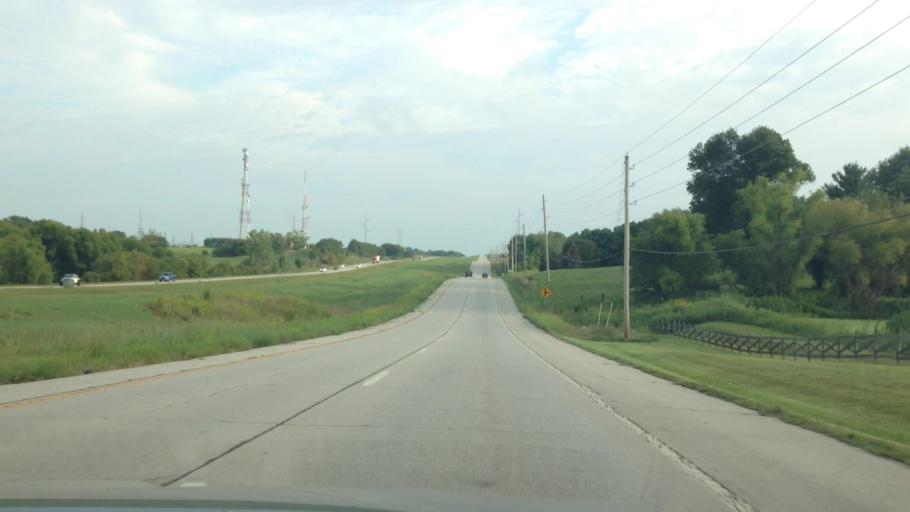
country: US
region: Missouri
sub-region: Clay County
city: Smithville
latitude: 39.3393
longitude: -94.5843
